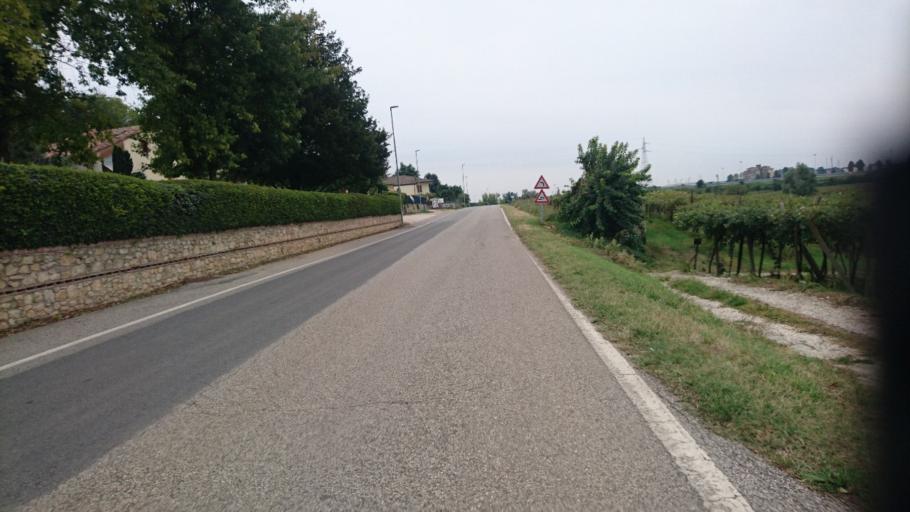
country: IT
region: Veneto
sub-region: Provincia di Verona
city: Soave
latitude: 45.4131
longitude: 11.2544
